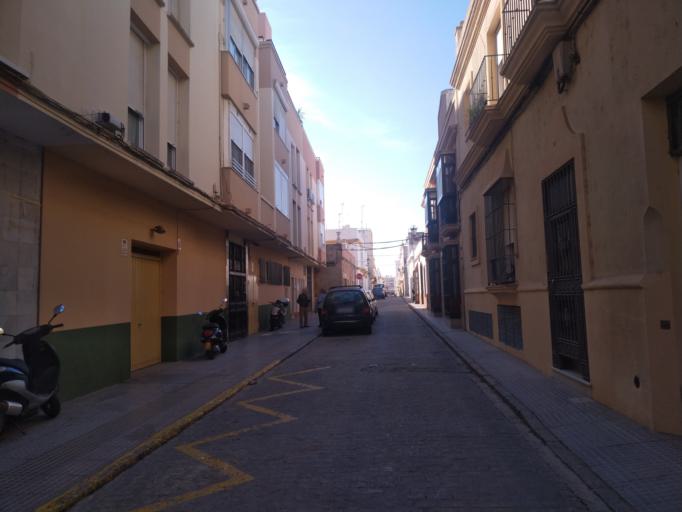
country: ES
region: Andalusia
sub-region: Provincia de Cadiz
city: San Fernando
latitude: 36.4662
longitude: -6.1930
